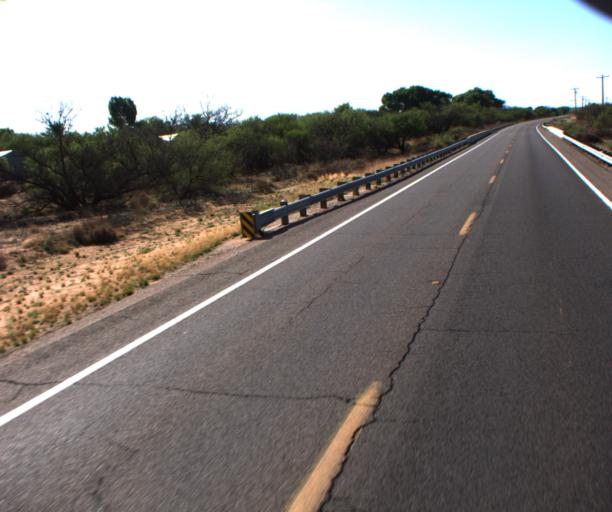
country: US
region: Arizona
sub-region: Cochise County
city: Saint David
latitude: 31.8758
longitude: -110.2104
